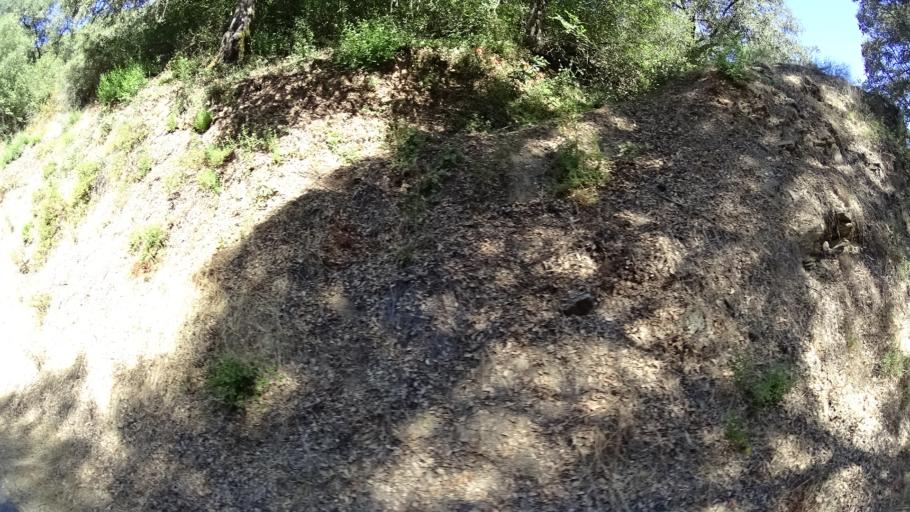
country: US
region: California
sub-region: Amador County
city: Jackson
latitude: 38.2796
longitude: -120.7572
